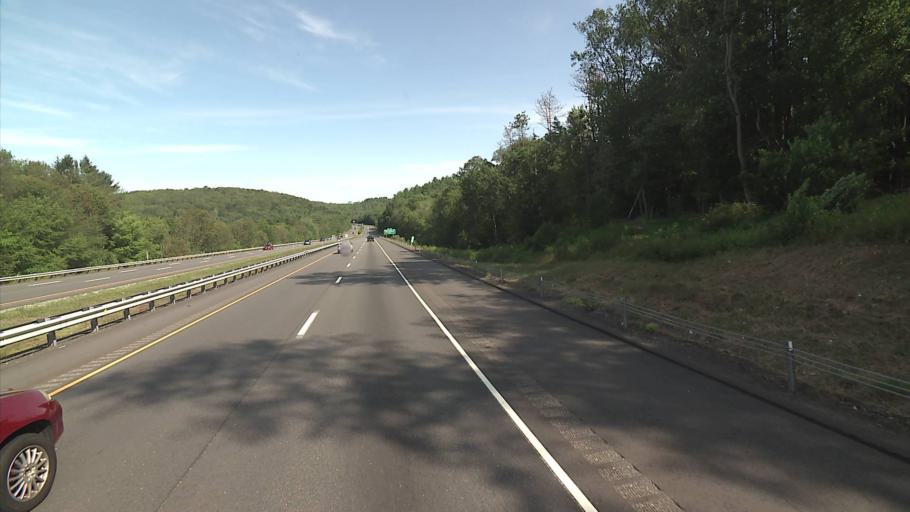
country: US
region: Connecticut
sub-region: Hartford County
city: Terramuggus
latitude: 41.5953
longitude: -72.4159
